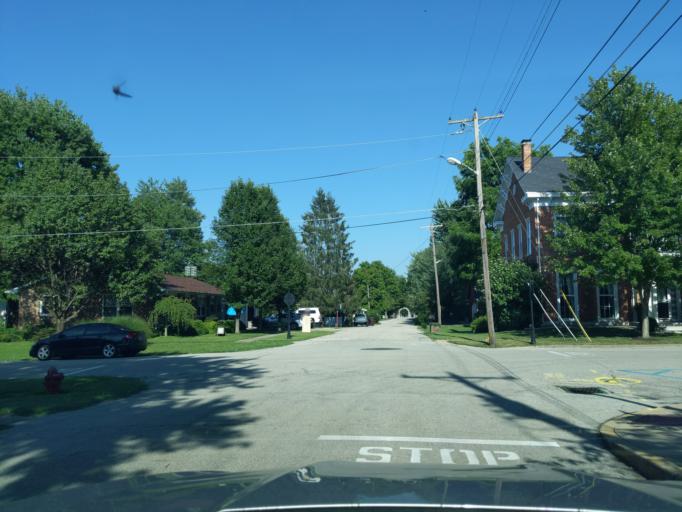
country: US
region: Indiana
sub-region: Ripley County
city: Versailles
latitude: 39.0734
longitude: -85.2513
